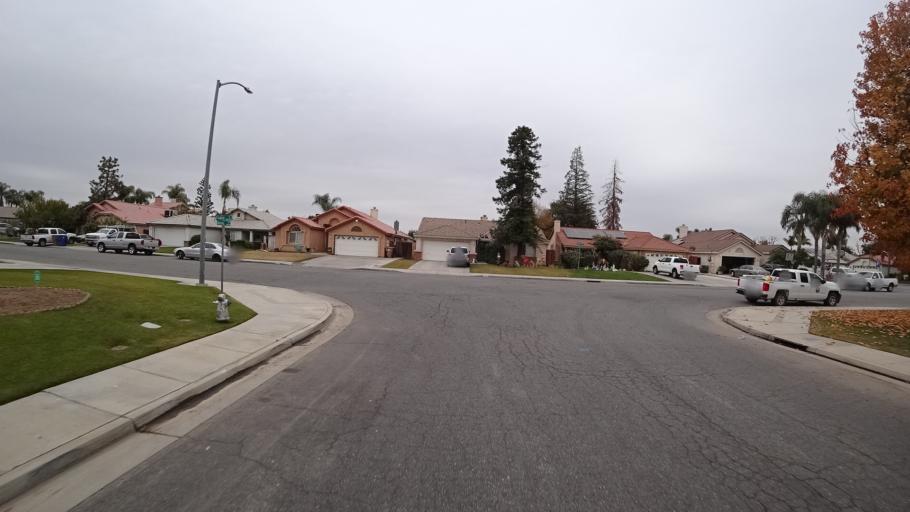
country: US
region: California
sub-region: Kern County
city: Greenfield
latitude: 35.2874
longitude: -119.0446
